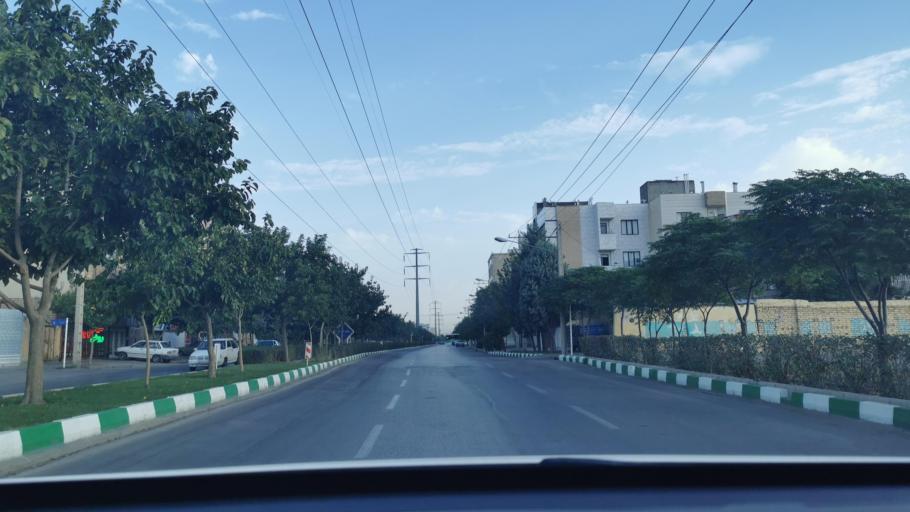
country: IR
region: Razavi Khorasan
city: Mashhad
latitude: 36.3507
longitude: 59.5306
